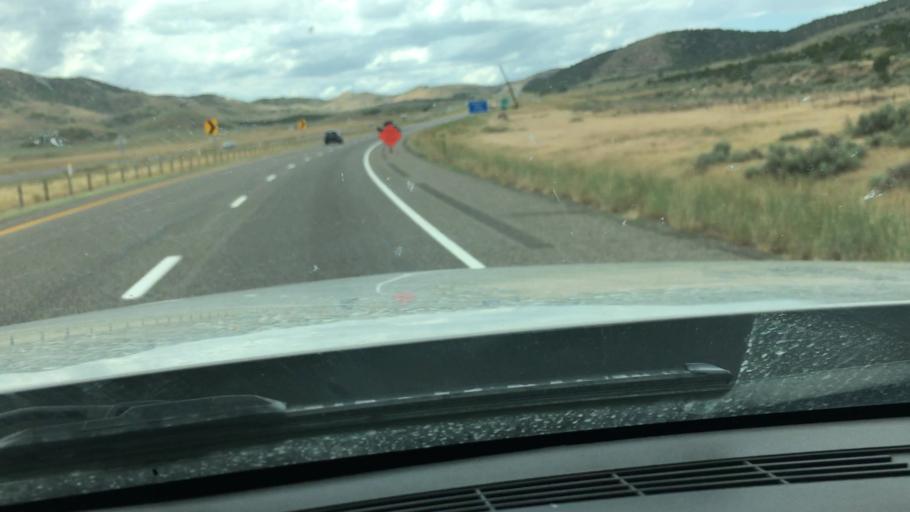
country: US
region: Utah
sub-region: Beaver County
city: Beaver
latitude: 38.6669
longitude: -112.5909
